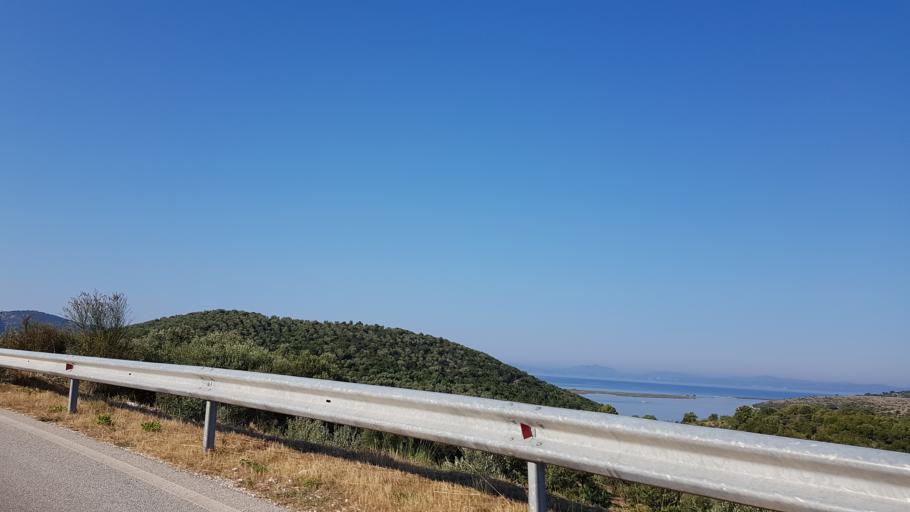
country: AL
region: Vlore
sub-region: Rrethi i Sarandes
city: Xarre
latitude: 39.7530
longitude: 20.0034
